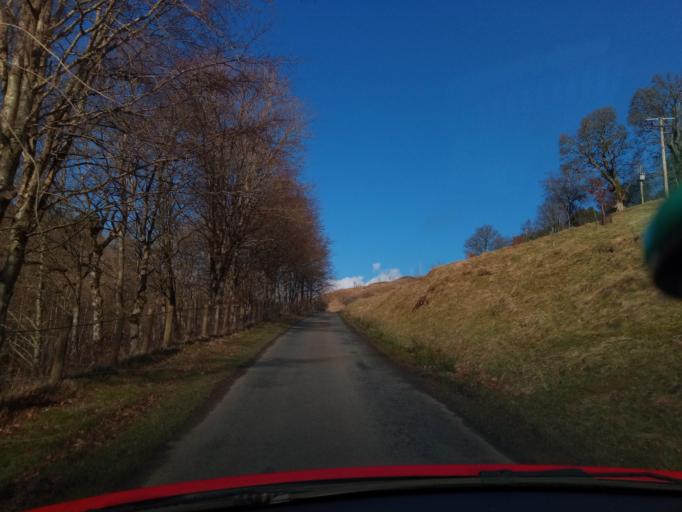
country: GB
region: Scotland
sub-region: The Scottish Borders
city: Hawick
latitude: 55.4238
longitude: -2.8728
